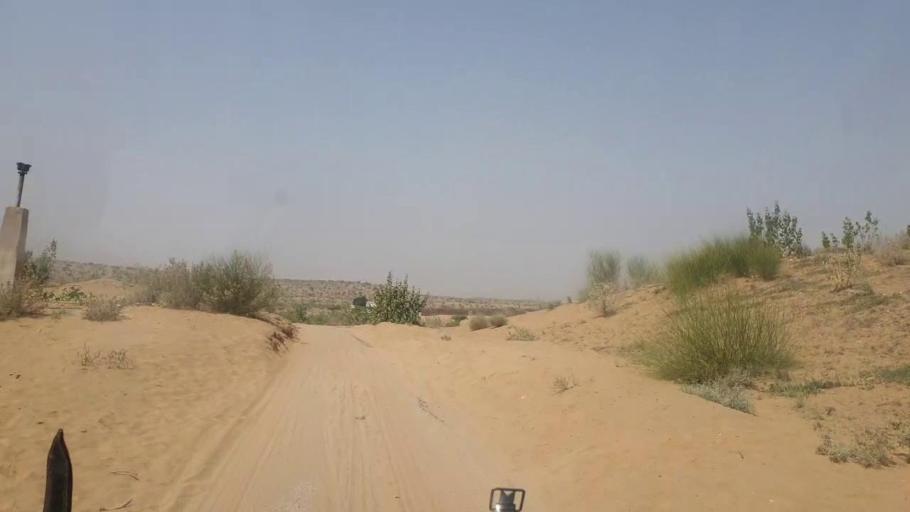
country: PK
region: Sindh
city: Islamkot
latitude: 25.1777
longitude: 70.1977
